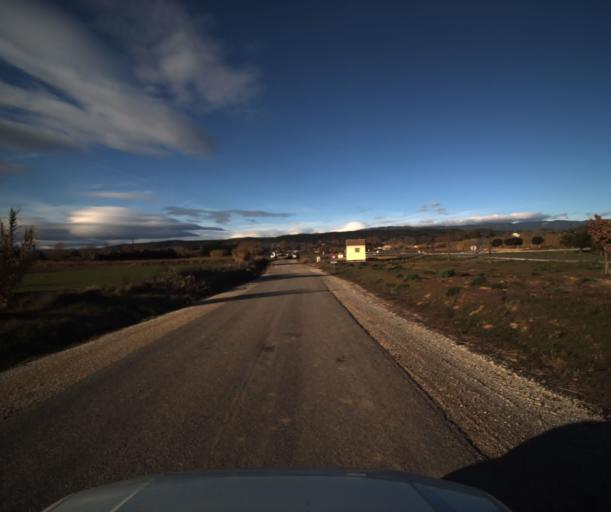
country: FR
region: Provence-Alpes-Cote d'Azur
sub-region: Departement du Vaucluse
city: Pertuis
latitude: 43.6866
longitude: 5.4830
